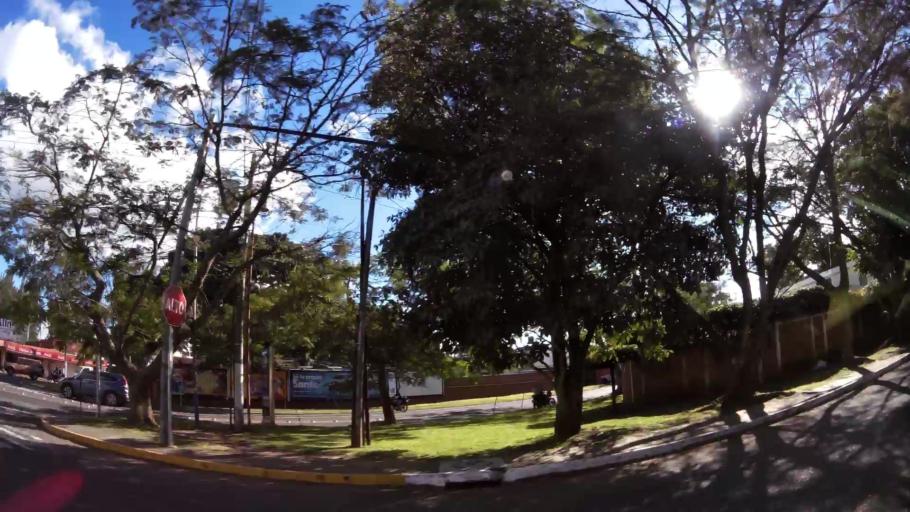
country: GT
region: Guatemala
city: Guatemala City
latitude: 14.6063
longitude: -90.5499
